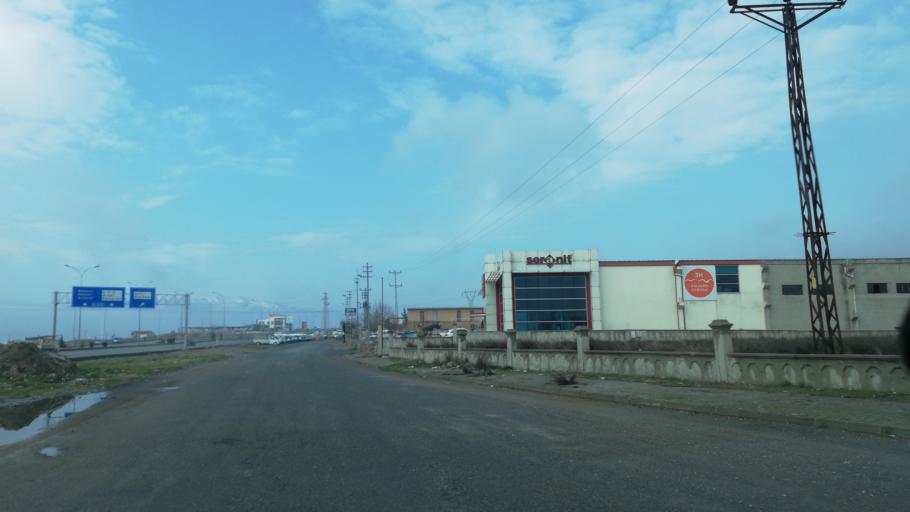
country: TR
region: Kahramanmaras
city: Kahramanmaras
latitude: 37.5642
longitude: 36.8952
